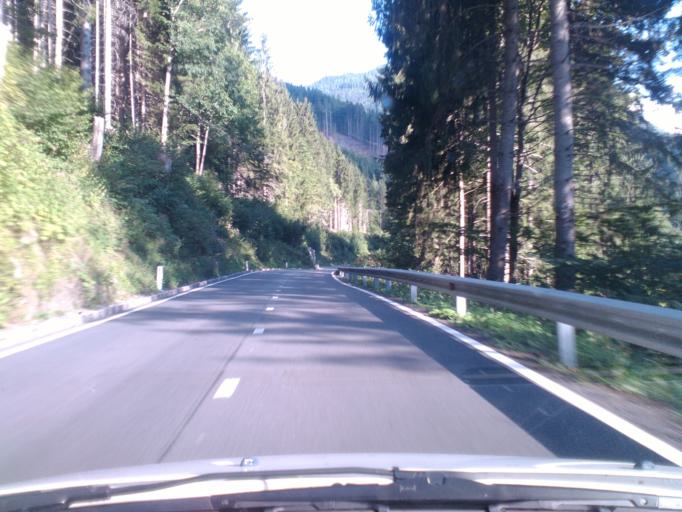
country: AT
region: Carinthia
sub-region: Politischer Bezirk Villach Land
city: Arnoldstein
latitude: 46.5323
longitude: 13.7491
